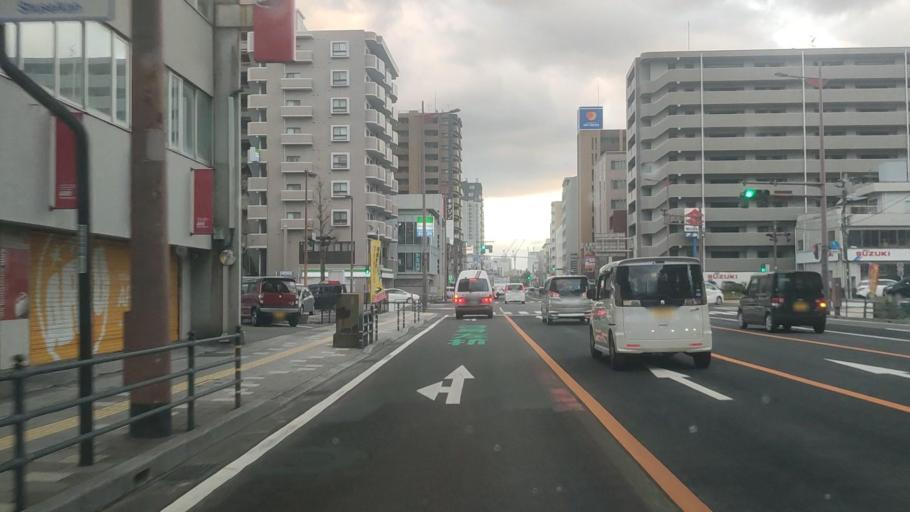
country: JP
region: Kagoshima
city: Kagoshima-shi
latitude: 31.5908
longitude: 130.5457
